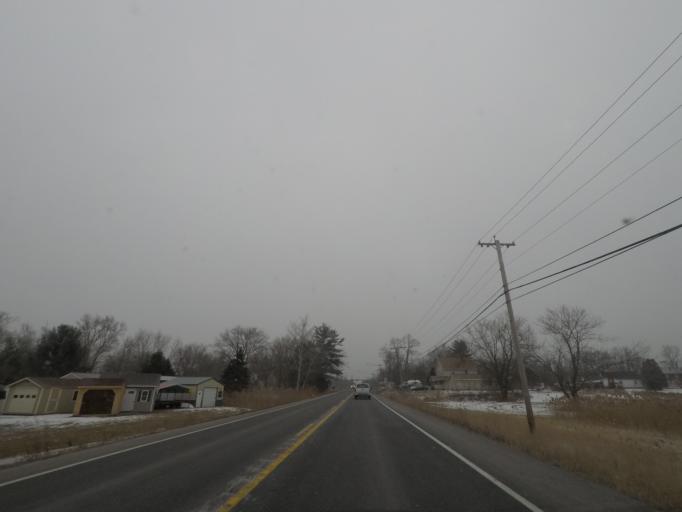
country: US
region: New York
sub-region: Rensselaer County
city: Castleton-on-Hudson
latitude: 42.5504
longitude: -73.8079
